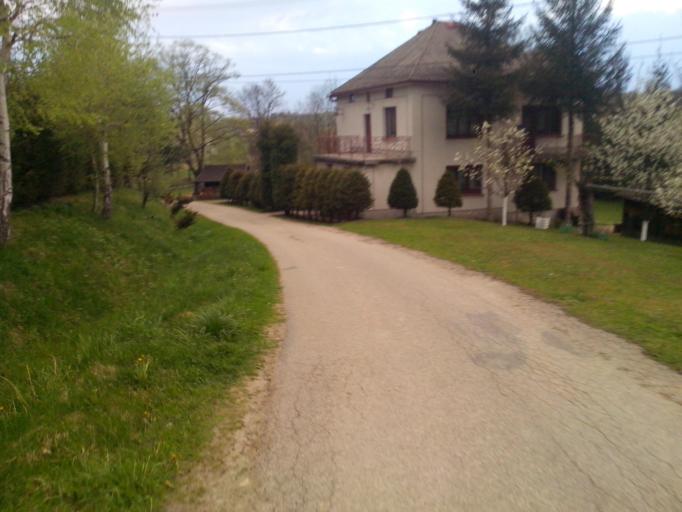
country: PL
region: Subcarpathian Voivodeship
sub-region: Powiat strzyzowski
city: Strzyzow
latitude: 49.8371
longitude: 21.8034
